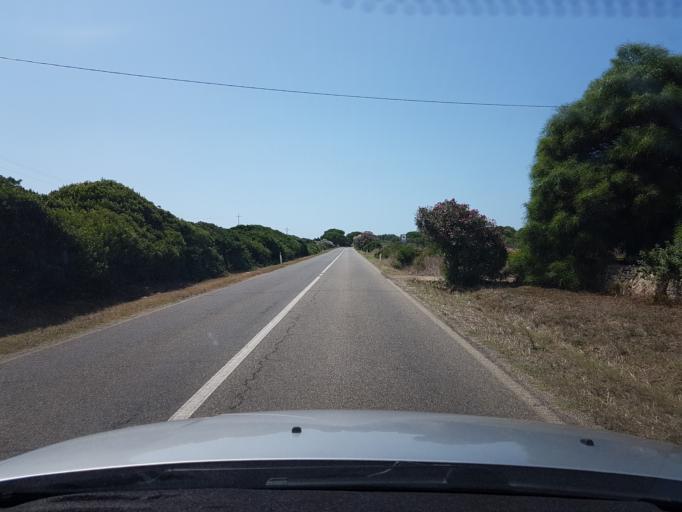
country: IT
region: Sardinia
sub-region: Provincia di Oristano
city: Riola Sardo
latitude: 40.0216
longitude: 8.4572
